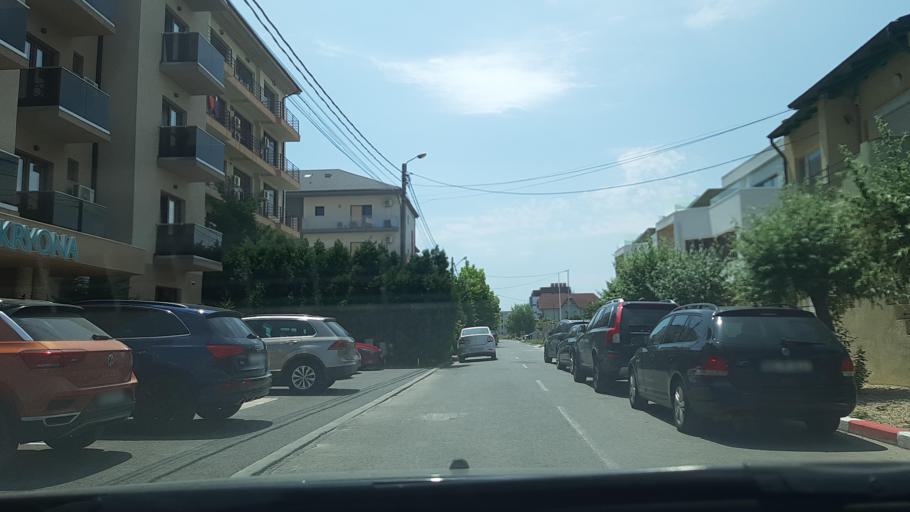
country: RO
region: Constanta
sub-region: Comuna Navodari
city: Navodari
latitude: 44.3027
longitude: 28.6223
